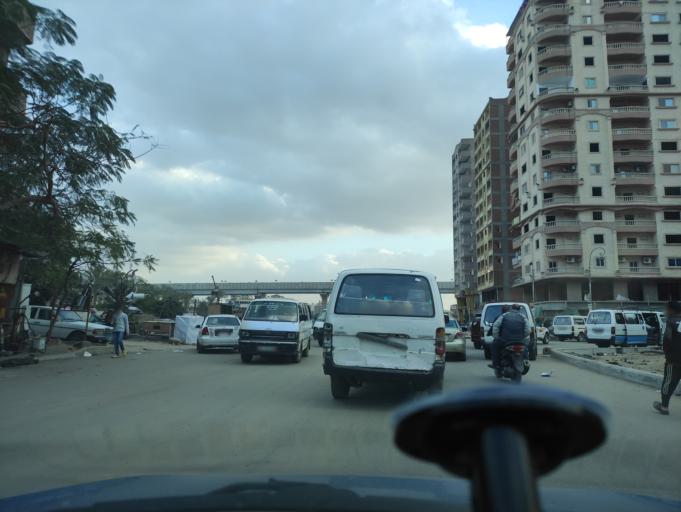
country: EG
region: Muhafazat al Qalyubiyah
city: Al Khankah
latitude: 30.1301
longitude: 31.3612
